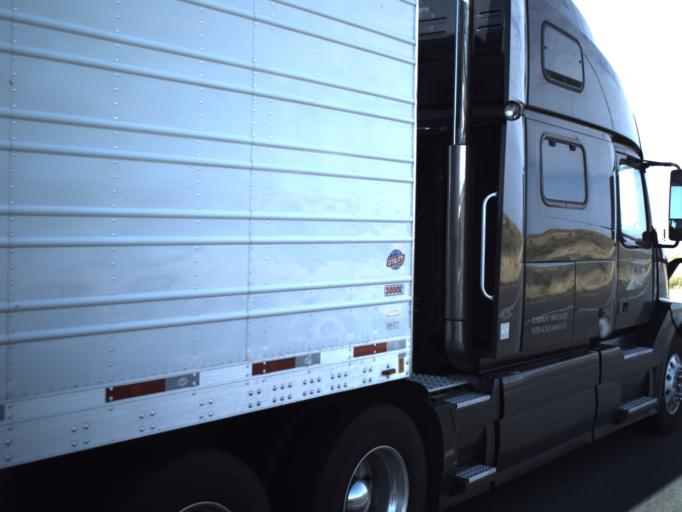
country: US
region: Utah
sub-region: Tooele County
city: Grantsville
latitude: 40.6873
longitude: -112.4522
